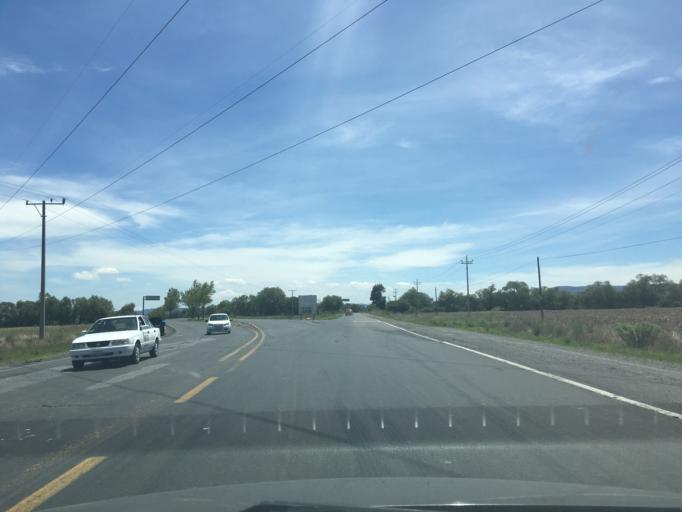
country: MX
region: Hidalgo
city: Huichapan
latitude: 20.3348
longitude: -99.6934
